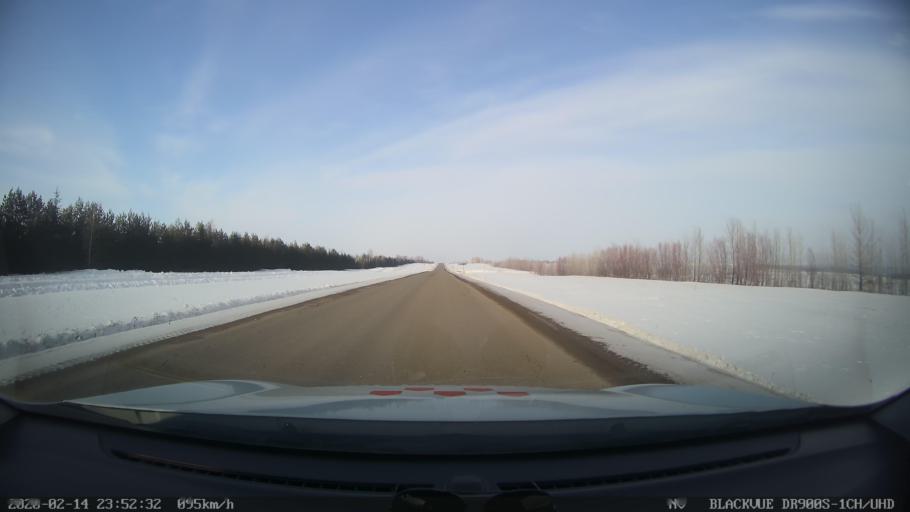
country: RU
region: Tatarstan
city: Kuybyshevskiy Zaton
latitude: 55.2802
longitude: 49.1437
